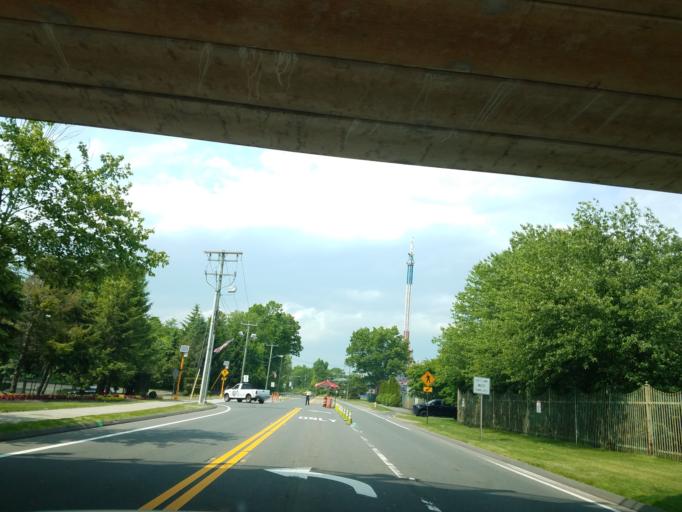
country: US
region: Massachusetts
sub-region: Hampden County
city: Agawam
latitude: 42.0378
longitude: -72.6164
